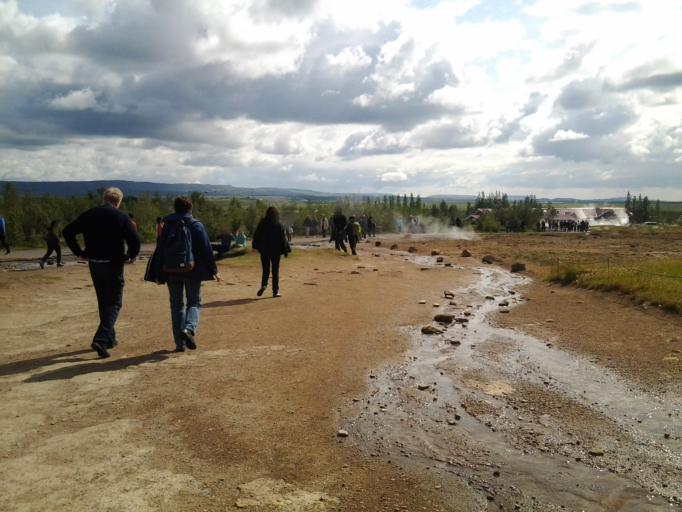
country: IS
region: South
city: Selfoss
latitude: 64.3123
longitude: -20.3013
